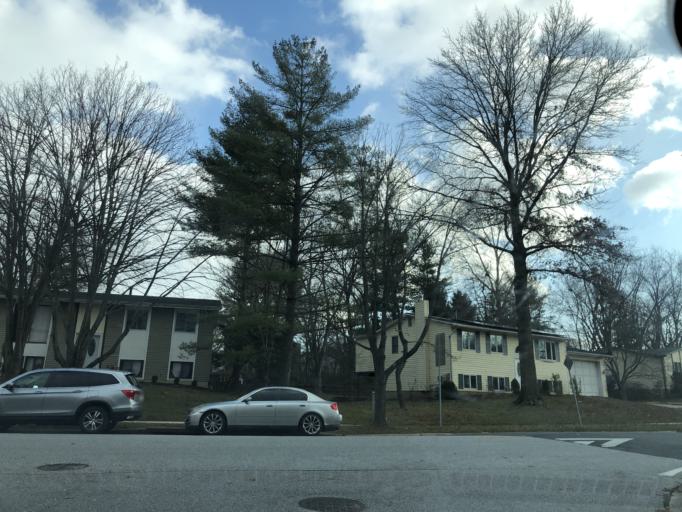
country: US
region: Maryland
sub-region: Howard County
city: Columbia
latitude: 39.2029
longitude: -76.8387
